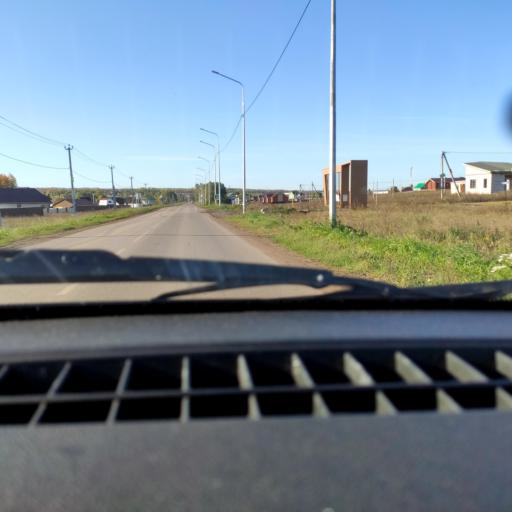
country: RU
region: Bashkortostan
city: Avdon
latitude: 54.5552
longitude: 55.7604
